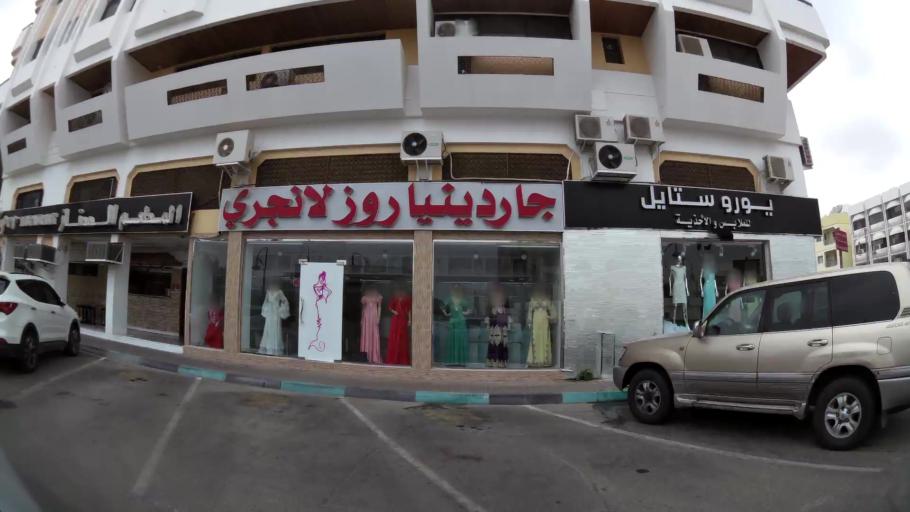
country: AE
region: Abu Dhabi
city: Al Ain
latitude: 24.2244
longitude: 55.7650
